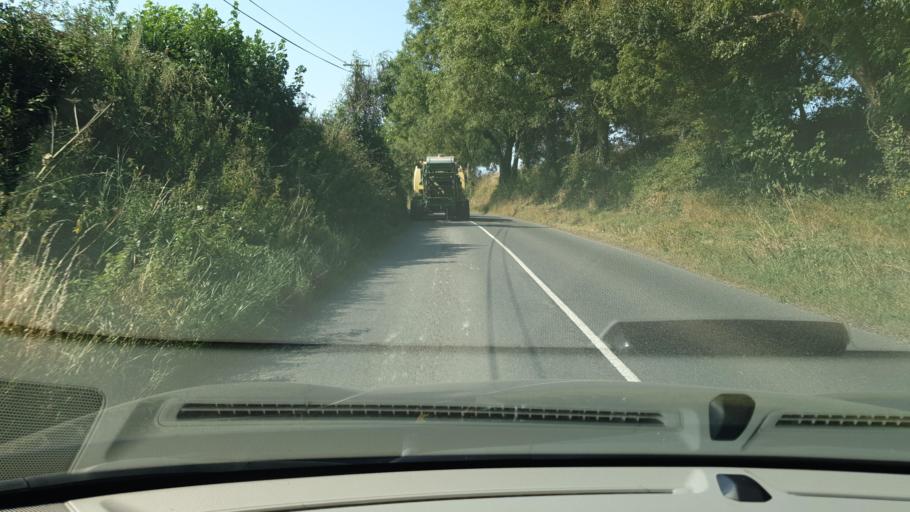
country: IE
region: Leinster
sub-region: An Mhi
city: Athboy
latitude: 53.5947
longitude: -6.8660
